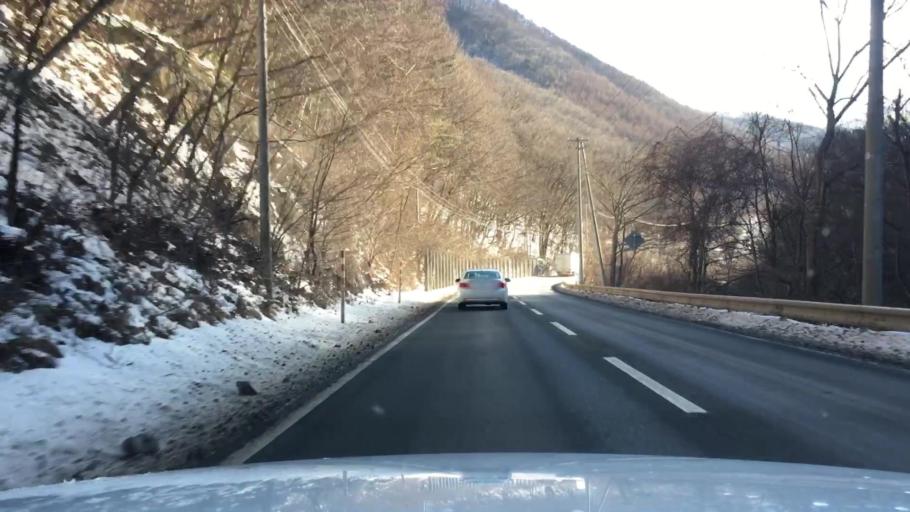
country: JP
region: Iwate
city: Tono
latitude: 39.6272
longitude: 141.4639
